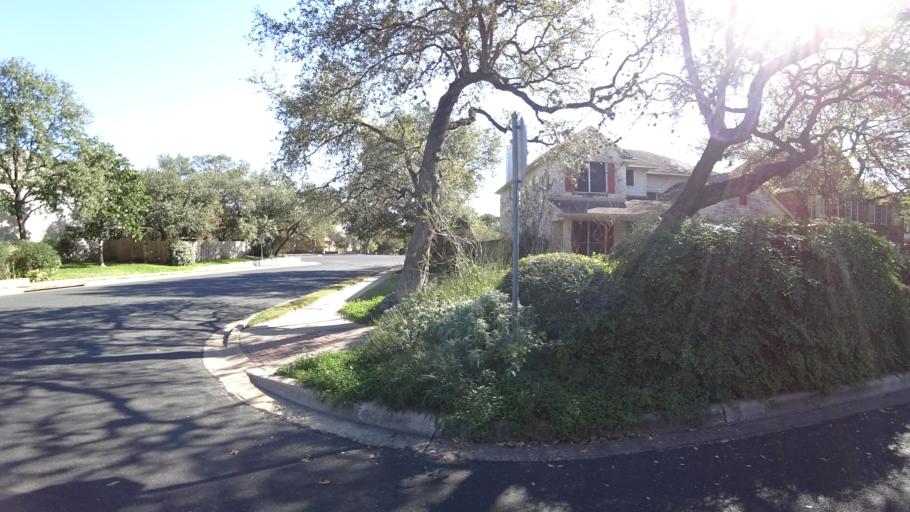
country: US
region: Texas
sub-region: Travis County
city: Shady Hollow
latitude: 30.2242
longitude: -97.8721
